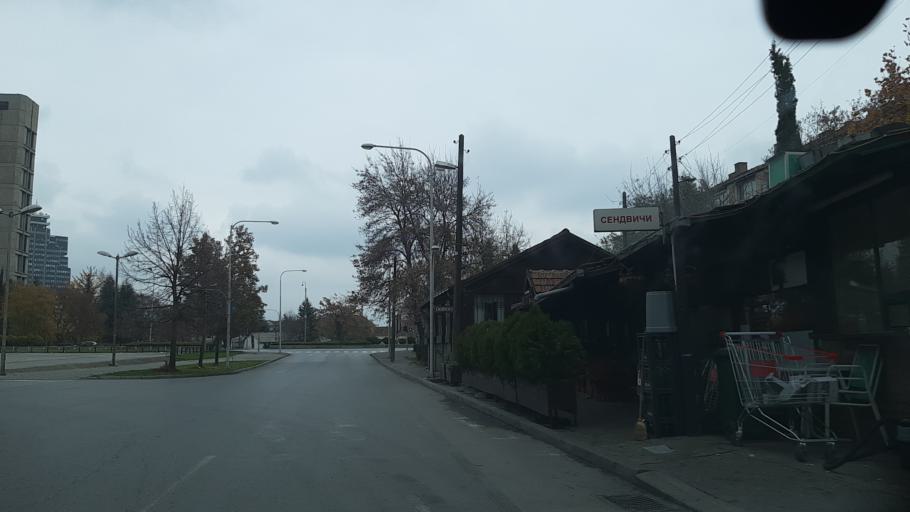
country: MK
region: Karpos
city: Skopje
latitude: 41.9922
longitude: 21.4425
